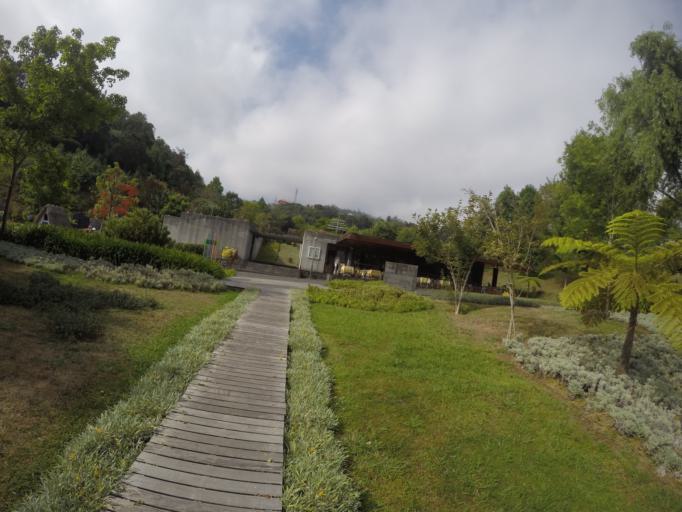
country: PT
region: Madeira
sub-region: Santana
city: Santana
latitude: 32.8029
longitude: -16.8850
